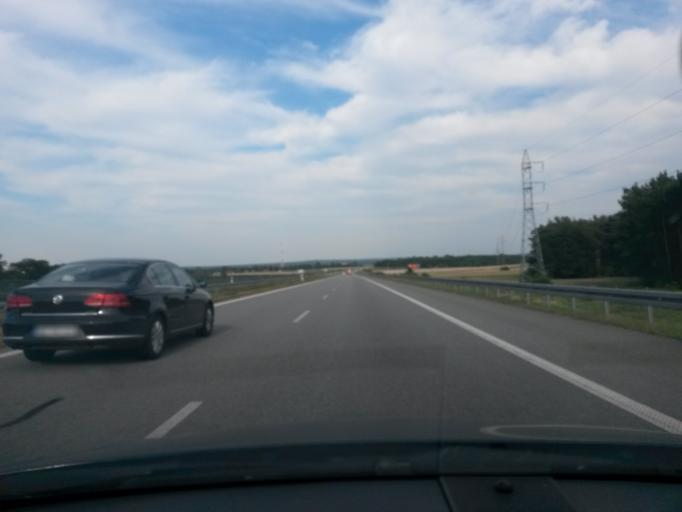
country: PL
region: Greater Poland Voivodeship
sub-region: Powiat koninski
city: Krzymow
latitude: 52.1406
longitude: 18.3659
